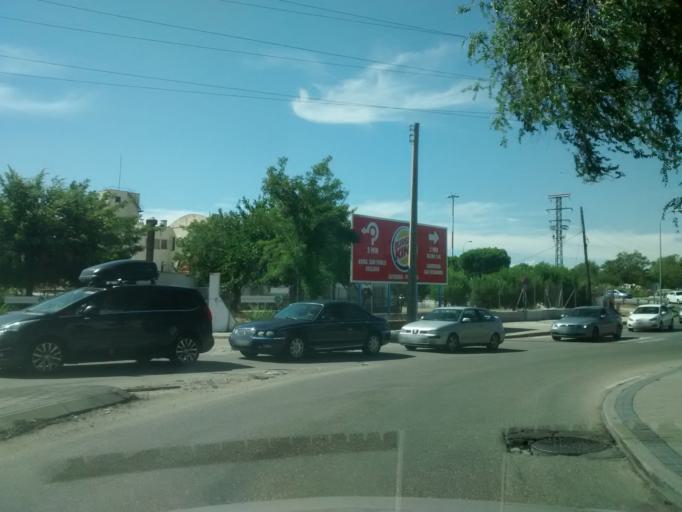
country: ES
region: Madrid
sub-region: Provincia de Madrid
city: San Fernando de Henares
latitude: 40.4452
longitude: -3.5332
